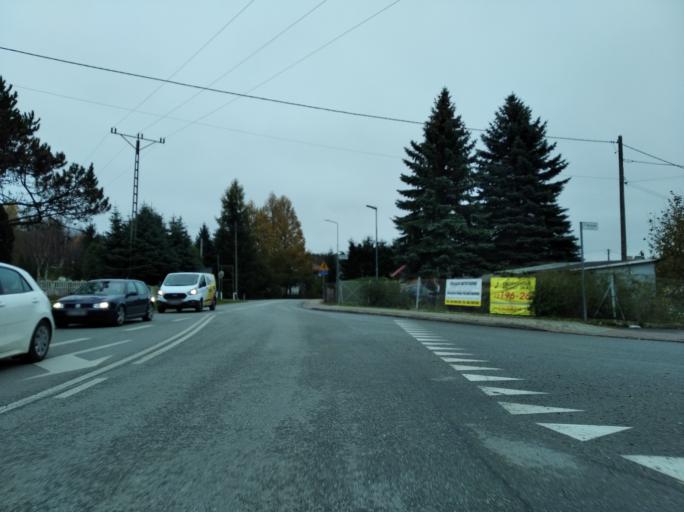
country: PL
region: Subcarpathian Voivodeship
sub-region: Krosno
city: Krosno
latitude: 49.7067
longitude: 21.7589
